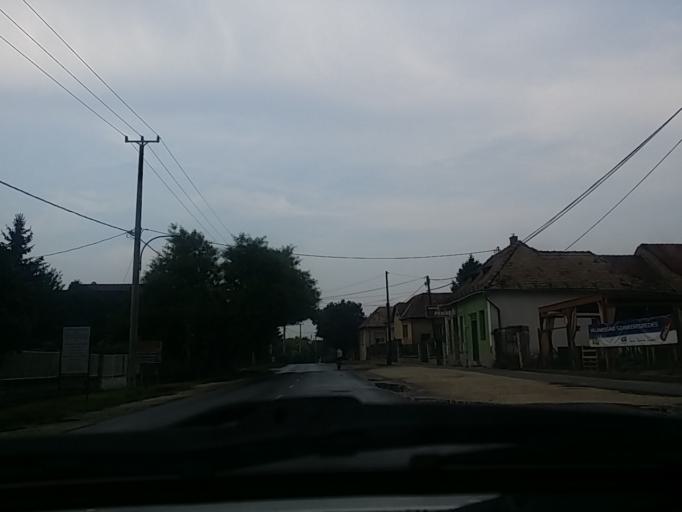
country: HU
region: Pest
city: Paty
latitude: 47.5135
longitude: 18.8237
